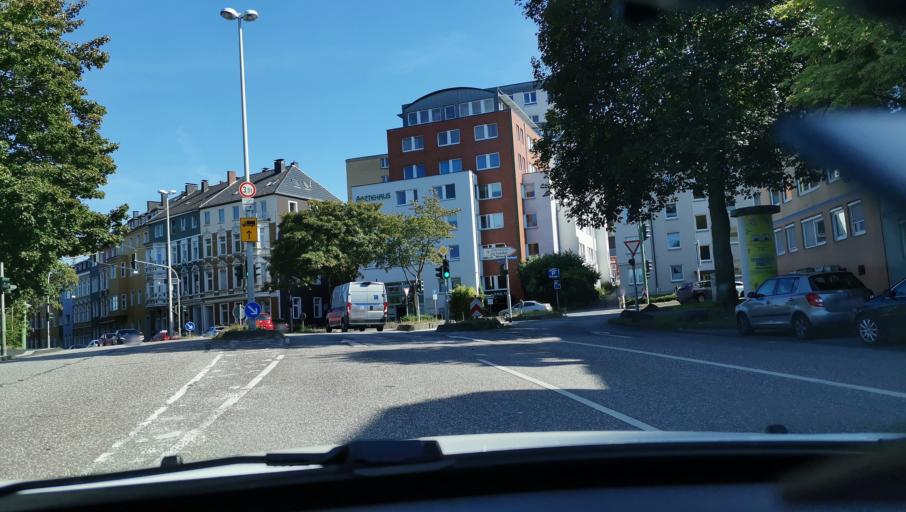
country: DE
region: North Rhine-Westphalia
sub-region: Regierungsbezirk Arnsberg
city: Hagen
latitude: 51.3561
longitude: 7.4654
